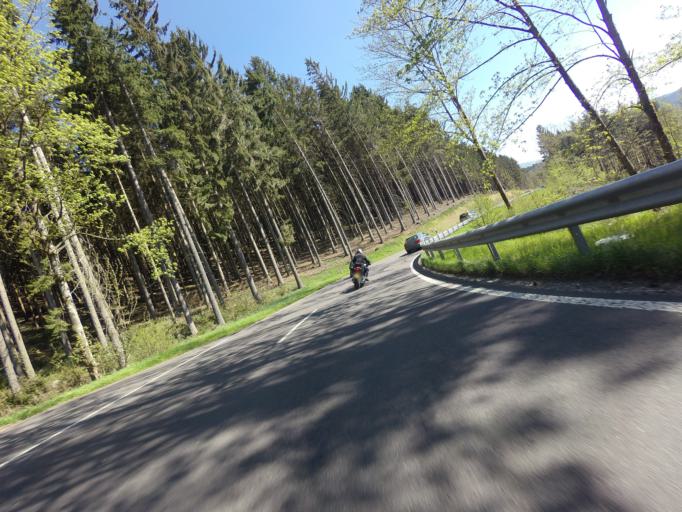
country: DE
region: North Rhine-Westphalia
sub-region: Regierungsbezirk Arnsberg
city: Lennestadt
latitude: 51.0978
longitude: 8.0491
